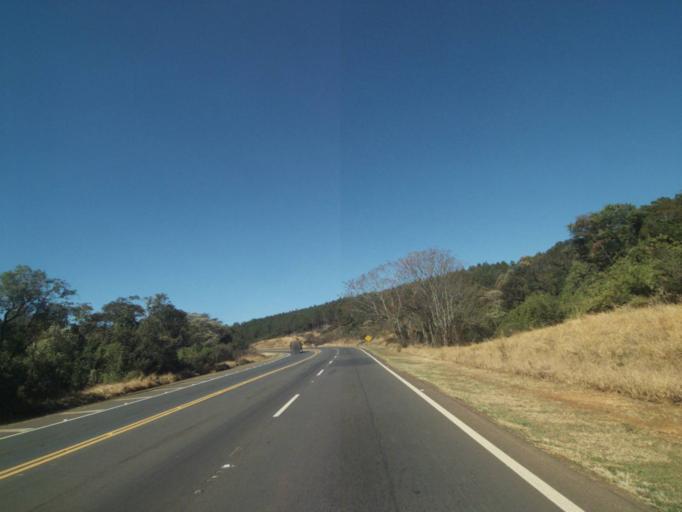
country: BR
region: Parana
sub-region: Tibagi
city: Tibagi
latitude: -24.7150
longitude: -50.5481
